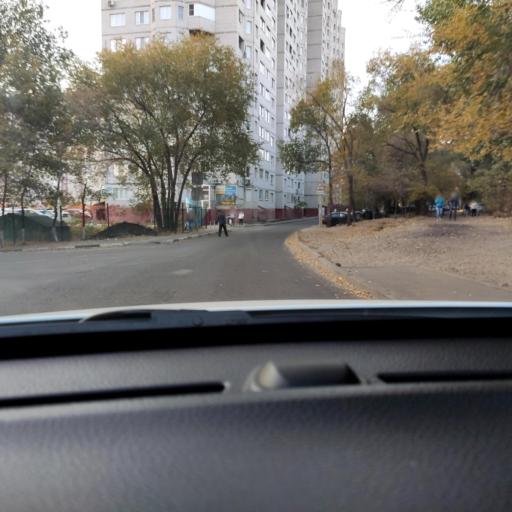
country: RU
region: Voronezj
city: Voronezh
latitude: 51.7141
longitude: 39.2710
